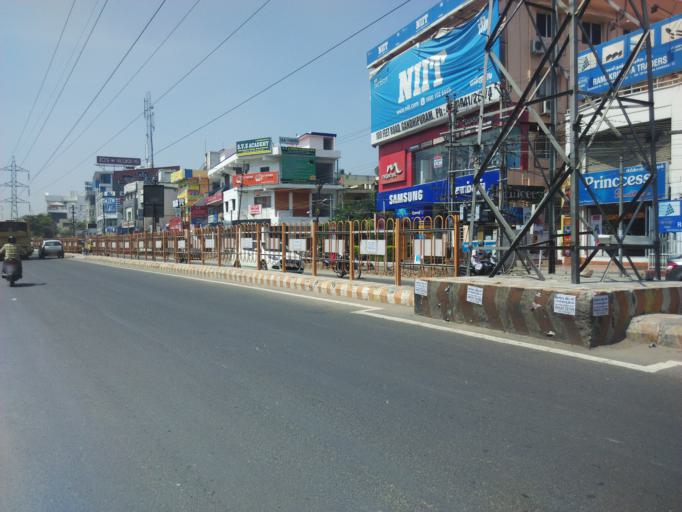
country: IN
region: Tamil Nadu
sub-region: Coimbatore
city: Coimbatore
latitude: 11.0195
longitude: 76.9640
